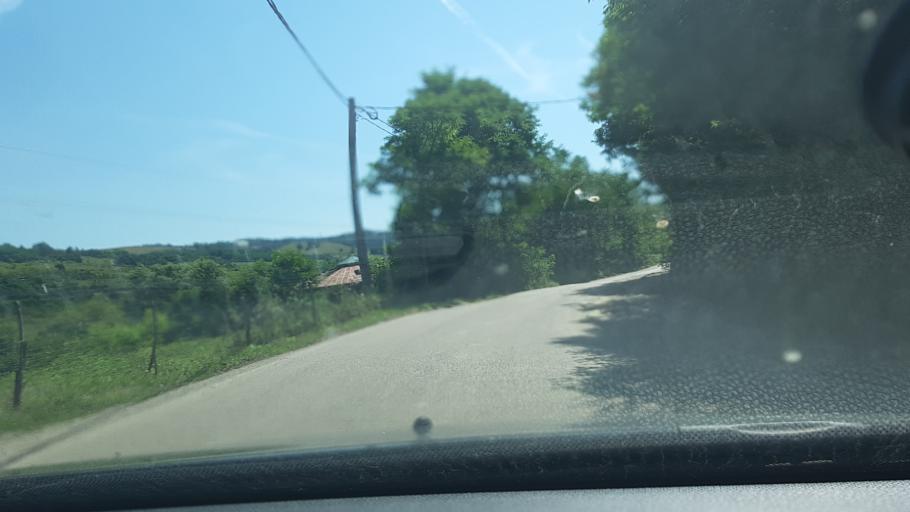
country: RO
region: Hunedoara
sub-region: Comuna Teliucu Inferior
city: Teliucu Inferior
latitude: 45.6897
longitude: 22.8670
